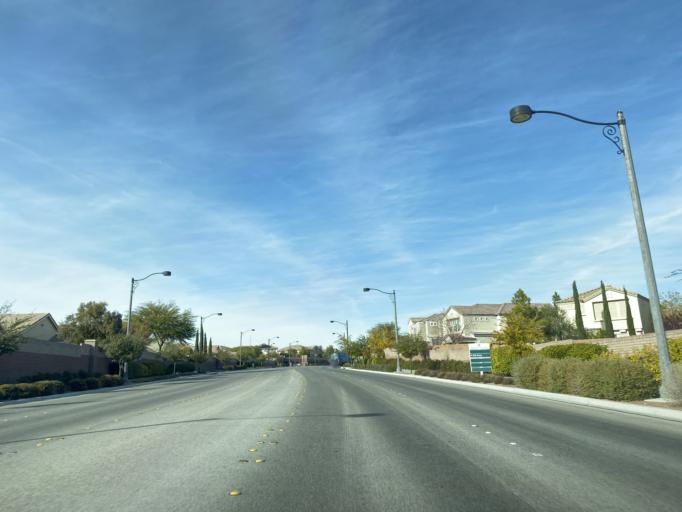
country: US
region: Nevada
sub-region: Clark County
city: Summerlin South
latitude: 36.3025
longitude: -115.3203
